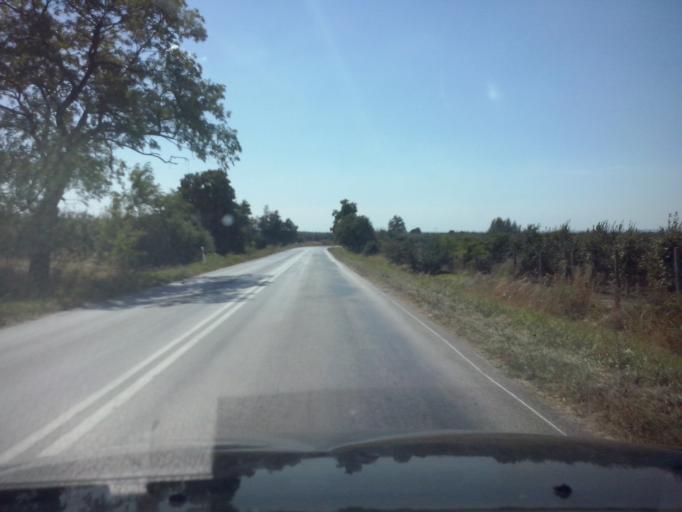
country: PL
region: Swietokrzyskie
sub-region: Powiat staszowski
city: Szydlow
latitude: 50.6088
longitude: 21.0092
